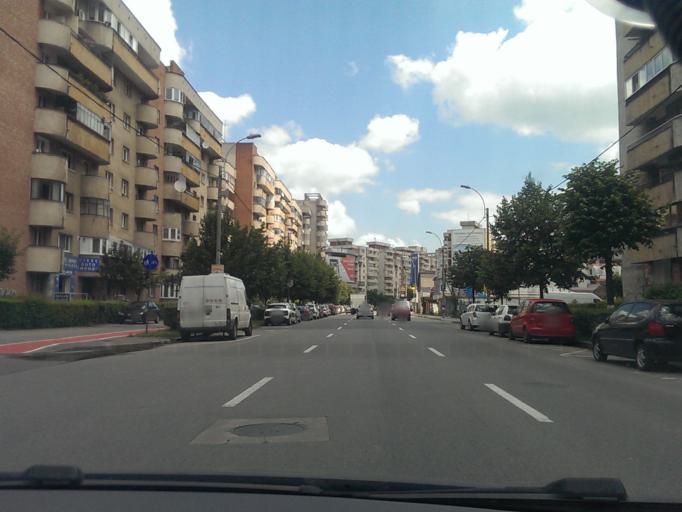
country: RO
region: Cluj
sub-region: Municipiul Cluj-Napoca
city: Cluj-Napoca
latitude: 46.7749
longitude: 23.6098
